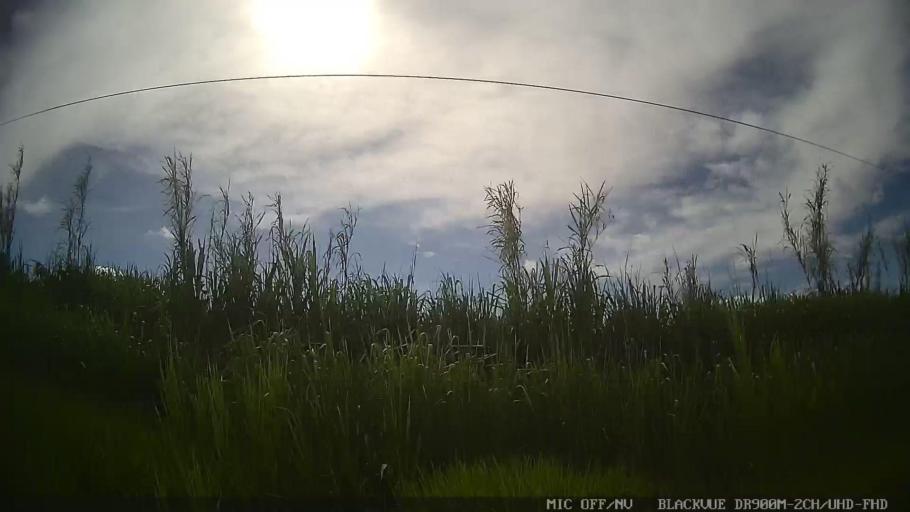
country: BR
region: Sao Paulo
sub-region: Conchas
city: Conchas
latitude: -22.9932
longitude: -47.9983
